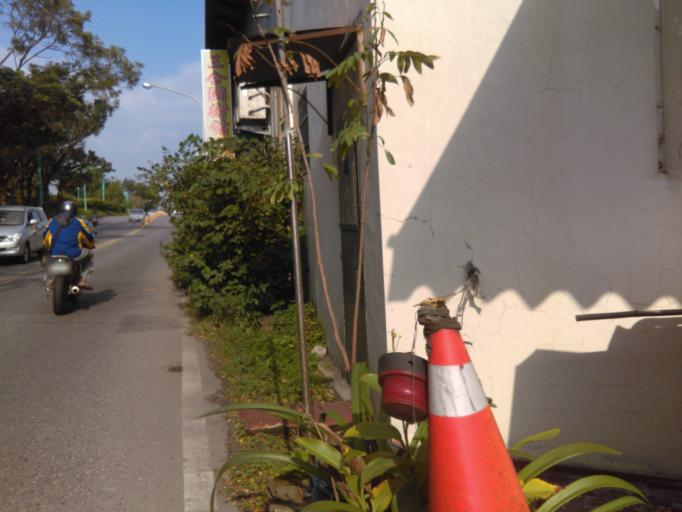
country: TW
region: Taiwan
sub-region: Yilan
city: Yilan
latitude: 24.7582
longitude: 121.7456
